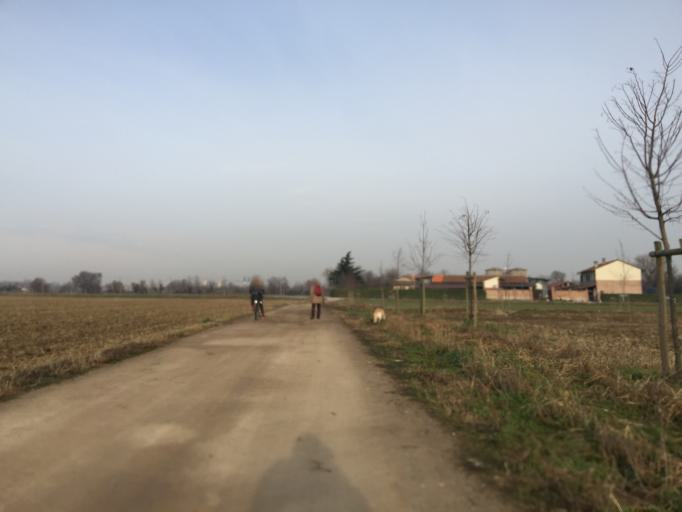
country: IT
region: Lombardy
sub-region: Citta metropolitana di Milano
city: Romano Banco
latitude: 45.4282
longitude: 9.1448
